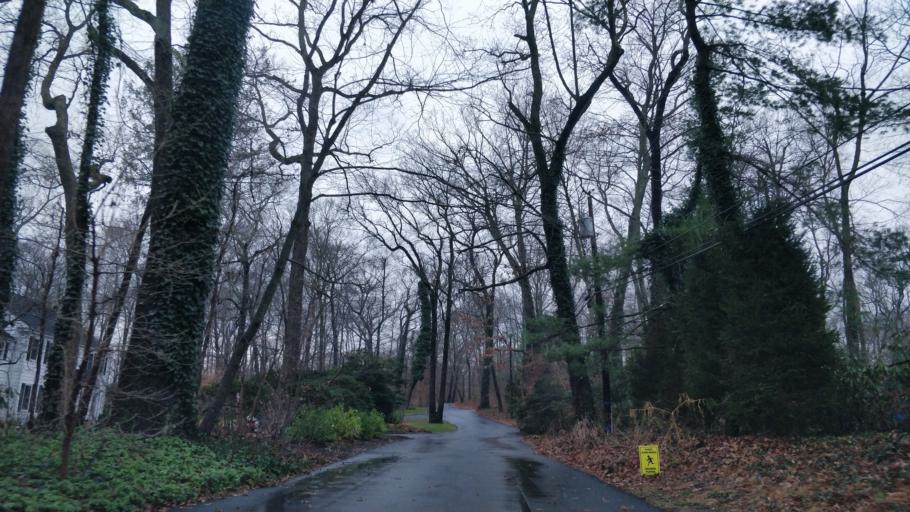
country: US
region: New York
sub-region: Nassau County
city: Upper Brookville
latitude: 40.8484
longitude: -73.5861
